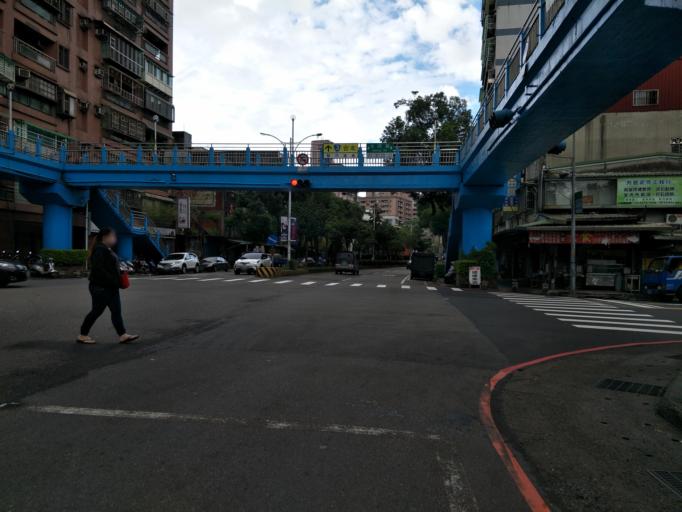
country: TW
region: Taiwan
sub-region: Taoyuan
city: Taoyuan
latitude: 24.9268
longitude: 121.3719
